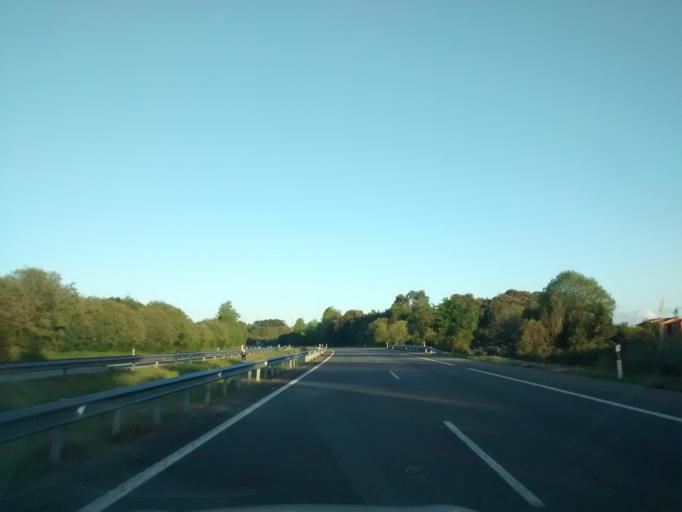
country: ES
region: Asturias
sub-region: Province of Asturias
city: Ribadesella
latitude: 43.4448
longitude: -4.9156
